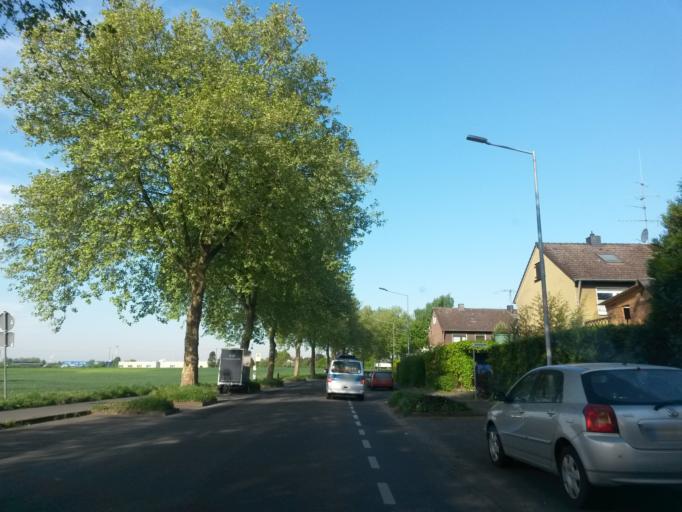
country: DE
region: North Rhine-Westphalia
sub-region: Regierungsbezirk Koln
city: Troisdorf
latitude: 50.7808
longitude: 7.1582
